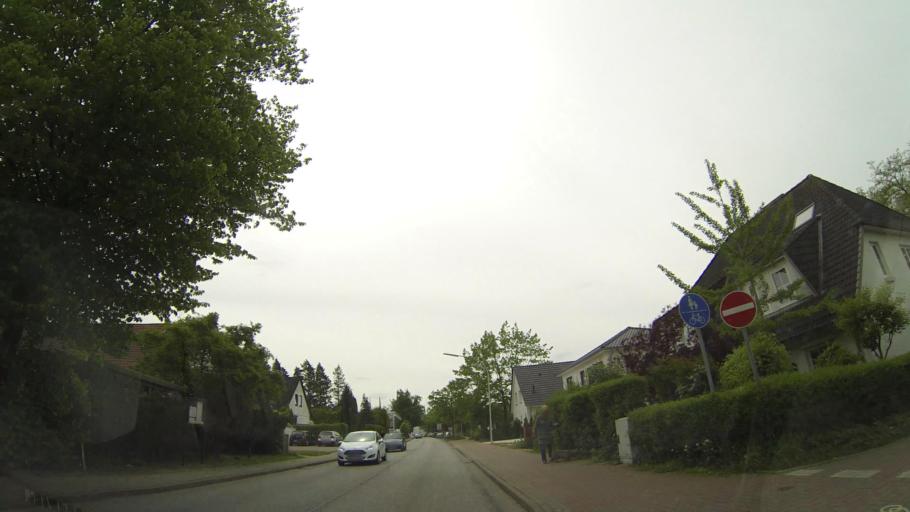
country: DE
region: Schleswig-Holstein
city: Halstenbek
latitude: 53.6115
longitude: 9.8401
